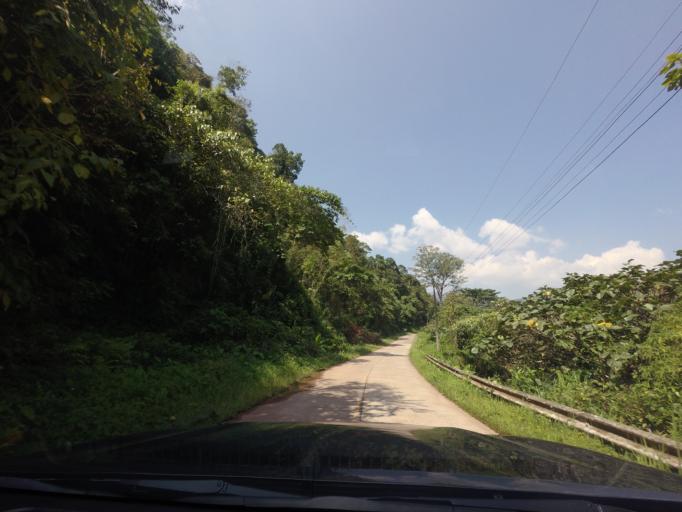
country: TH
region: Nan
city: Bo Kluea
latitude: 19.1950
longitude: 101.1925
